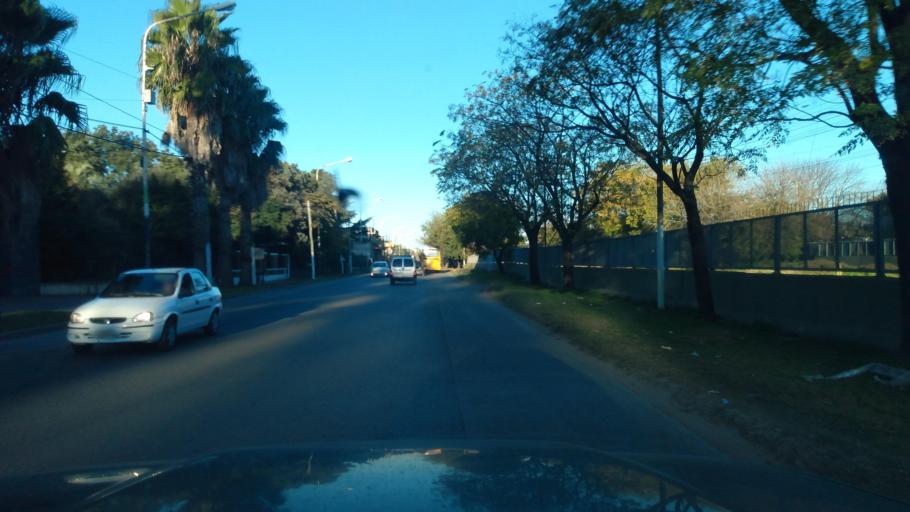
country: AR
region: Buenos Aires
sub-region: Partido de Merlo
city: Merlo
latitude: -34.6465
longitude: -58.8034
